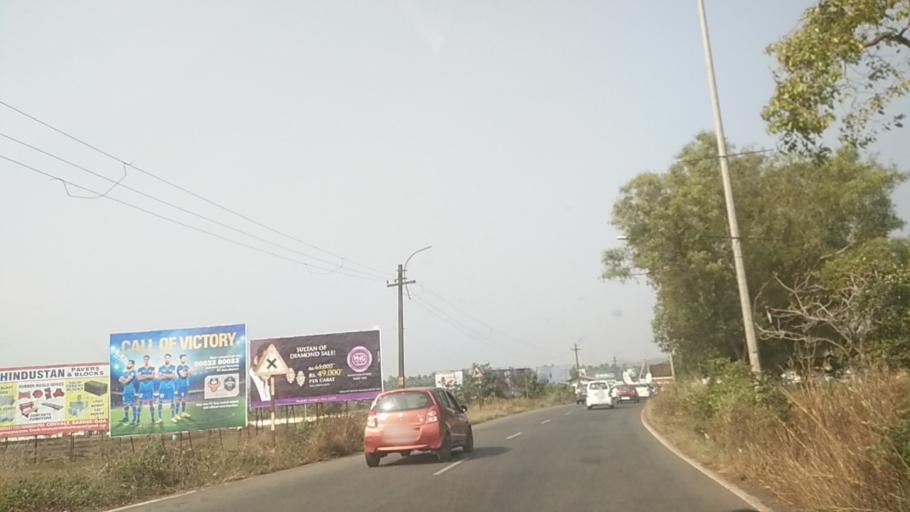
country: IN
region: Goa
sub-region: North Goa
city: Guirim
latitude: 15.5720
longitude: 73.8064
